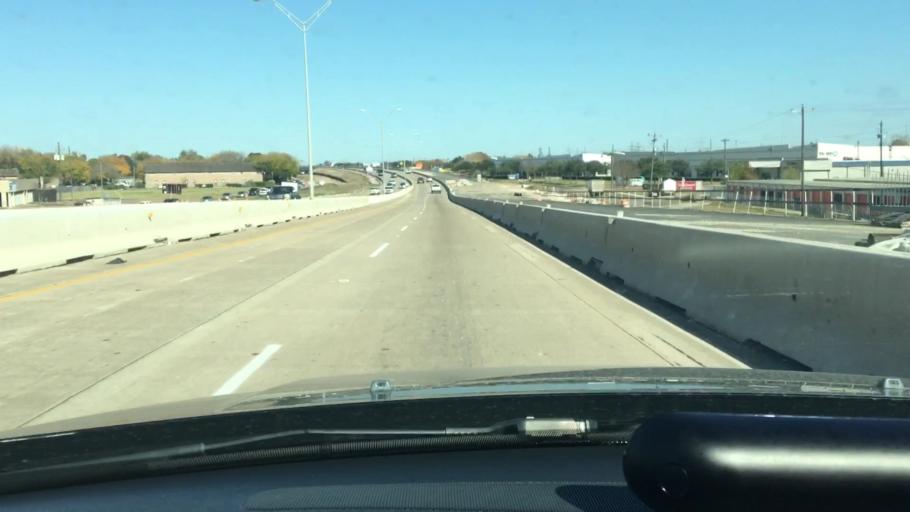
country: US
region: Texas
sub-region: Harris County
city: Deer Park
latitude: 29.6844
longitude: -95.1544
